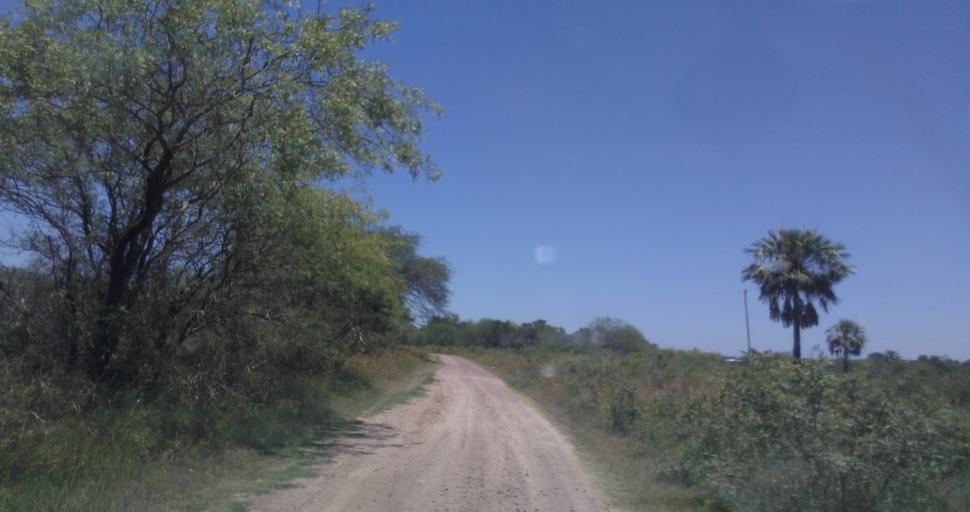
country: AR
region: Chaco
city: Fontana
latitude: -27.4822
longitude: -59.0621
